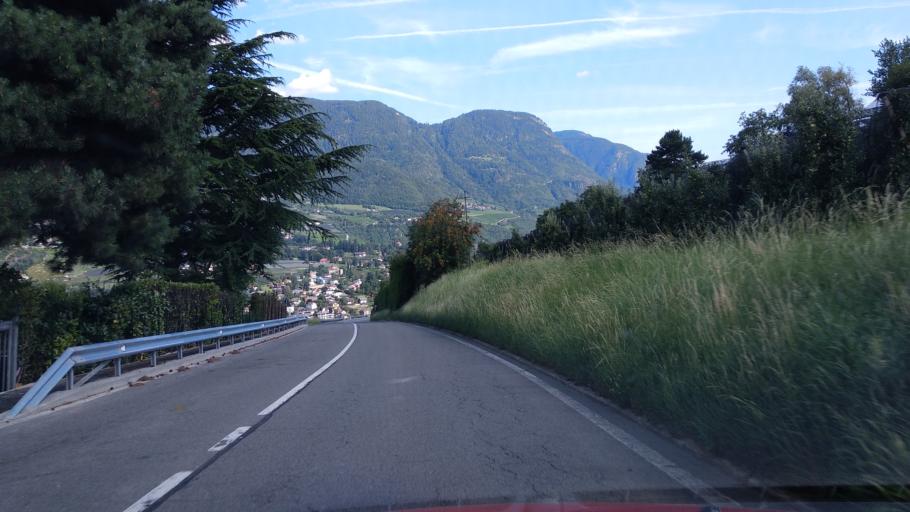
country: IT
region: Trentino-Alto Adige
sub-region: Bolzano
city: Tirolo
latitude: 46.6819
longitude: 11.1640
